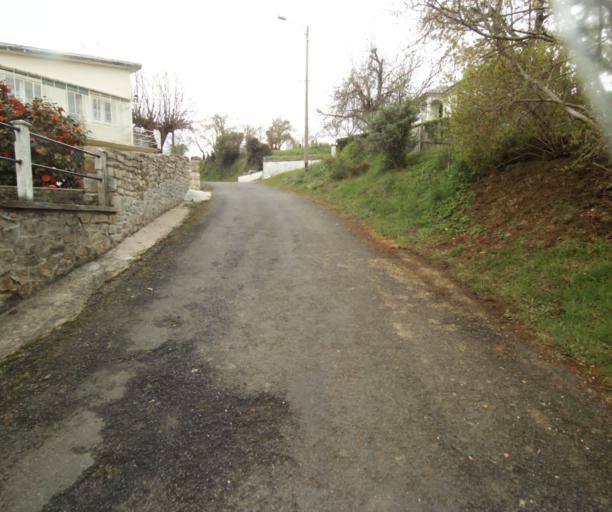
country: FR
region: Limousin
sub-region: Departement de la Correze
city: Naves
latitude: 45.2925
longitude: 1.8007
